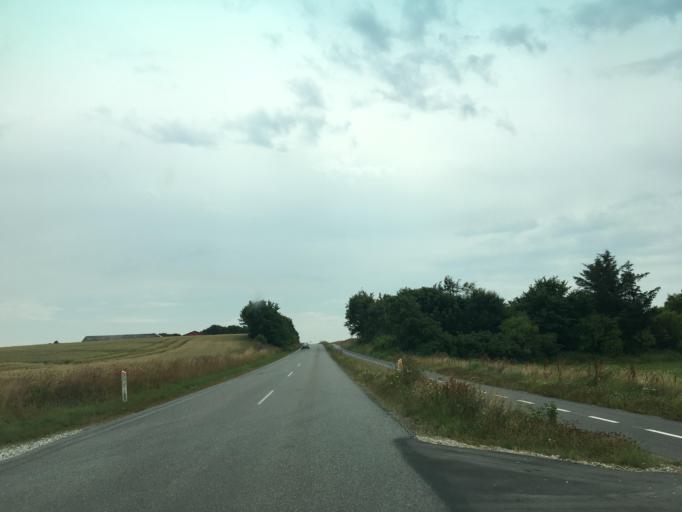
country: DK
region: North Denmark
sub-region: Thisted Kommune
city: Hurup
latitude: 56.7707
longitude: 8.4221
